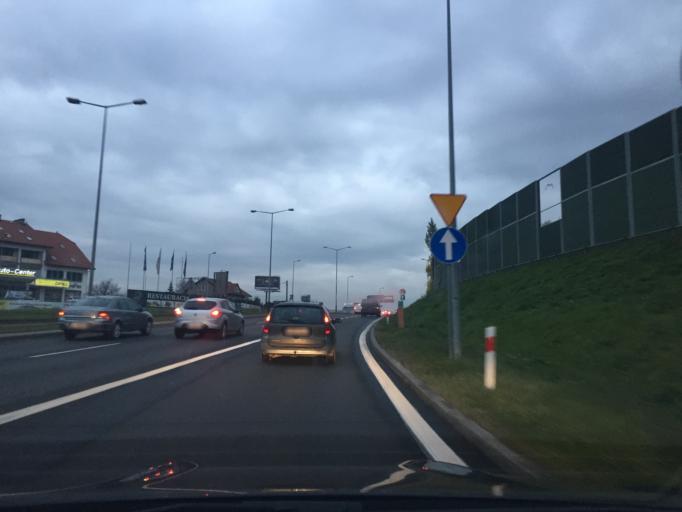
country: PL
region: Lesser Poland Voivodeship
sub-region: Powiat wielicki
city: Wieliczka
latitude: 50.0039
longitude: 20.0223
